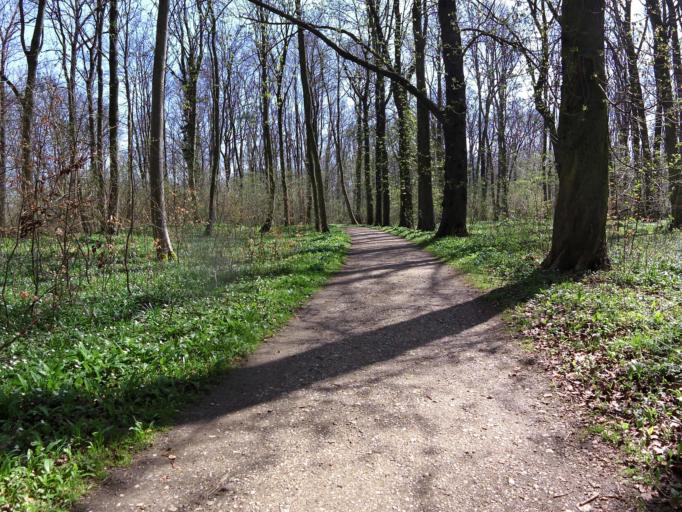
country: DE
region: Saxony
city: Schkeuditz
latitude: 51.3769
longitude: 12.2845
